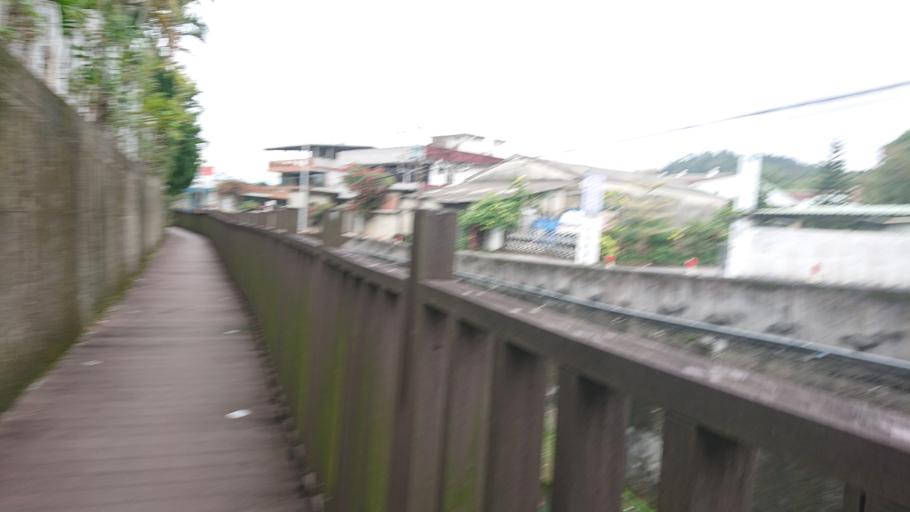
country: TW
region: Taipei
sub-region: Taipei
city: Banqiao
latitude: 24.9602
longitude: 121.4435
